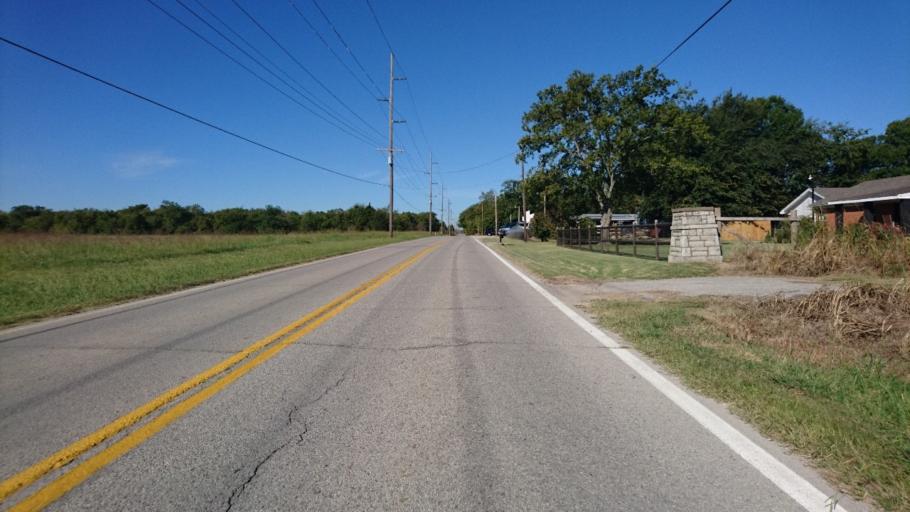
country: US
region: Oklahoma
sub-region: Rogers County
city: Catoosa
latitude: 36.1480
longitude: -95.7638
